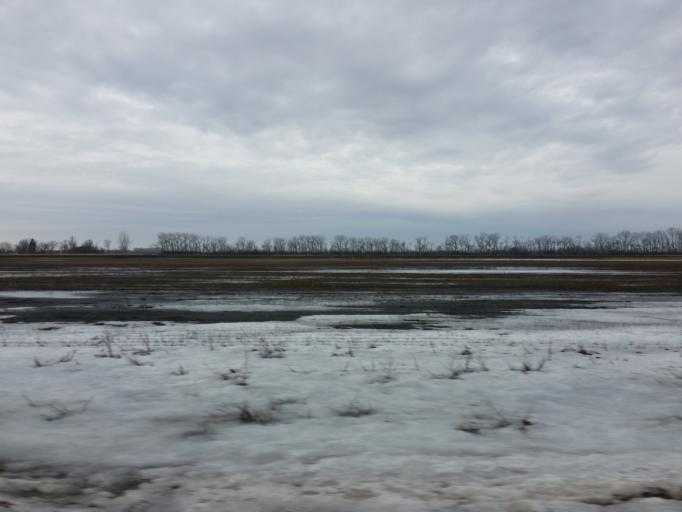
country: US
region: North Dakota
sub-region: Walsh County
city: Grafton
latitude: 48.3998
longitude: -97.4703
